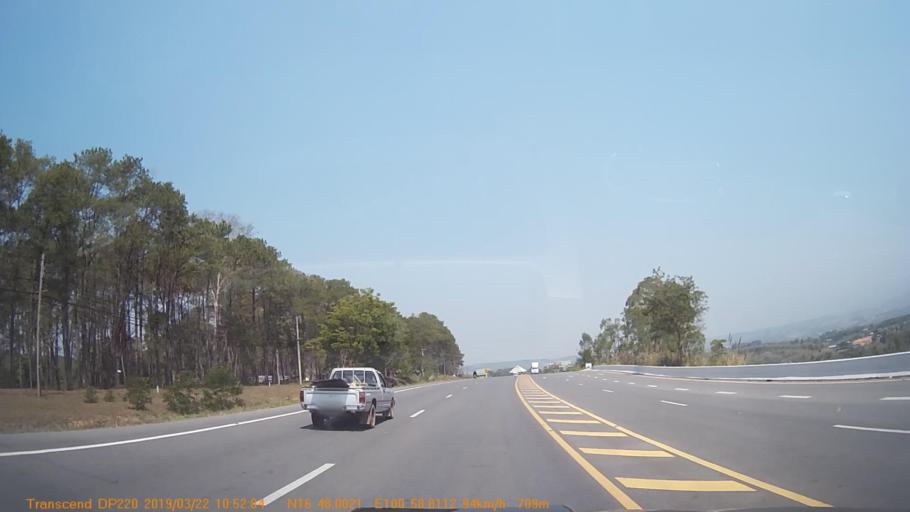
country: TH
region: Phetchabun
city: Khao Kho
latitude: 16.8000
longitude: 100.9798
